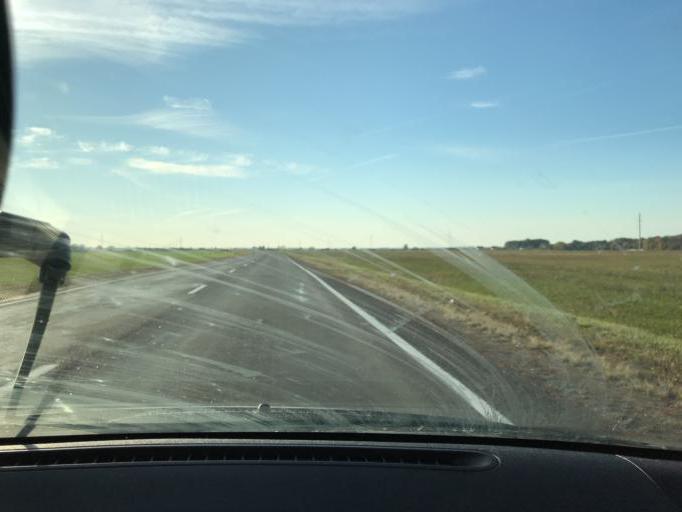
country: BY
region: Brest
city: Antopal'
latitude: 52.2259
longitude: 24.7354
